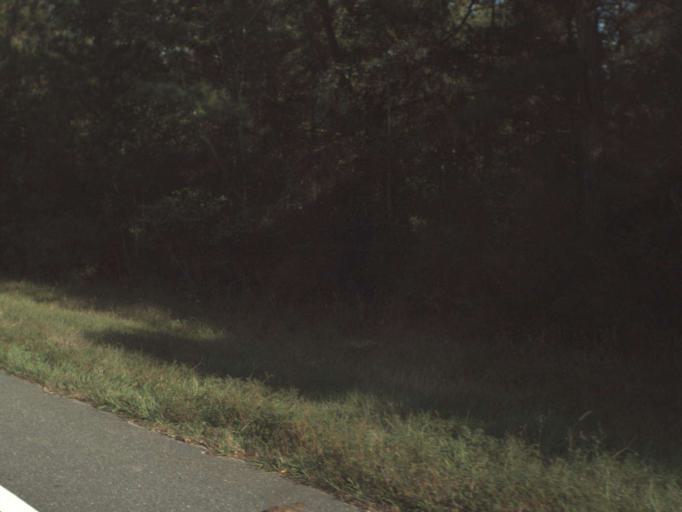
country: US
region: Florida
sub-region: Holmes County
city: Bonifay
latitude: 30.6575
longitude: -85.6600
